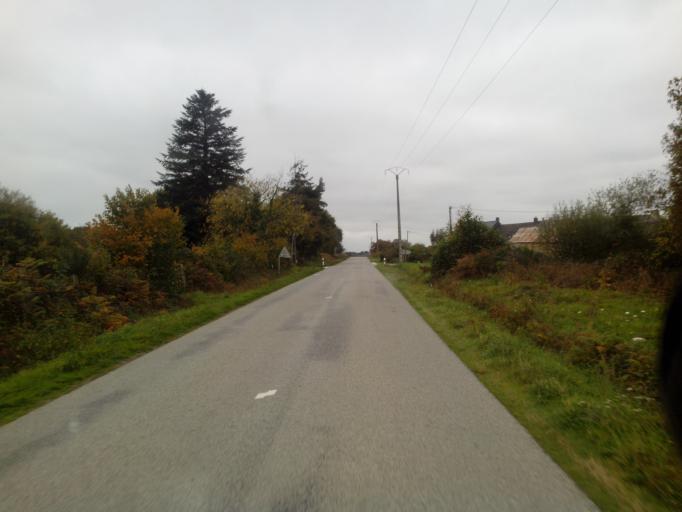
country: FR
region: Brittany
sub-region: Departement du Morbihan
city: Mauron
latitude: 48.0859
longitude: -2.3392
